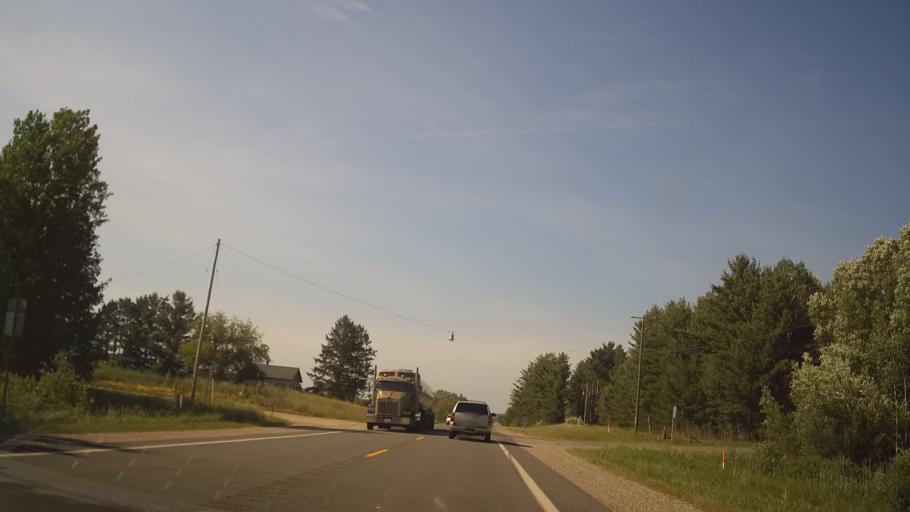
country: US
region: Michigan
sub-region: Ogemaw County
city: West Branch
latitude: 44.3920
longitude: -84.1163
